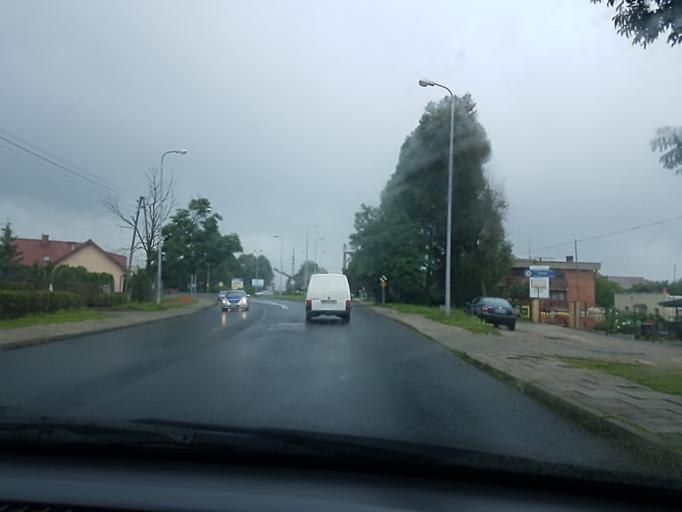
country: PL
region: Lodz Voivodeship
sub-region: Powiat kutnowski
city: Kutno
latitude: 52.2325
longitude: 19.3493
